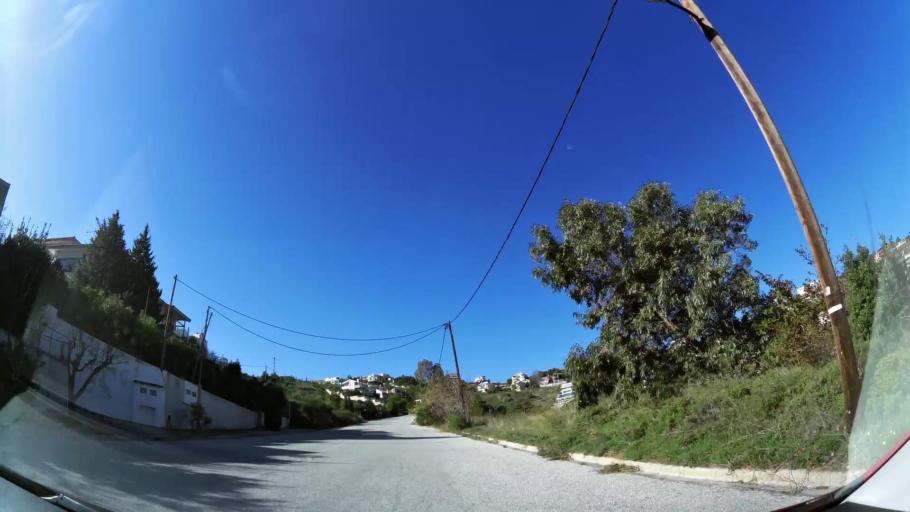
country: GR
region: Attica
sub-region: Nomarchia Anatolikis Attikis
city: Dhrafi
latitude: 38.0338
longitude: 23.8978
